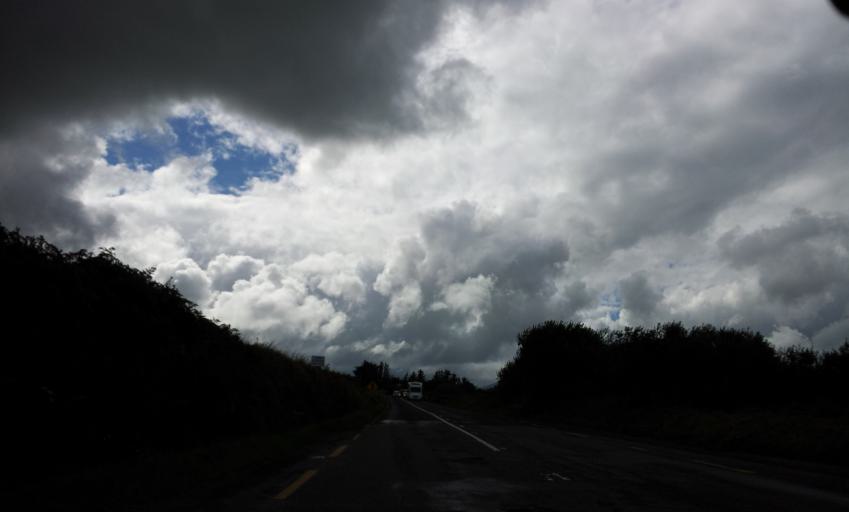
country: IE
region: Munster
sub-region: Ciarrai
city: Killorglin
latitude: 52.2333
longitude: -9.8580
